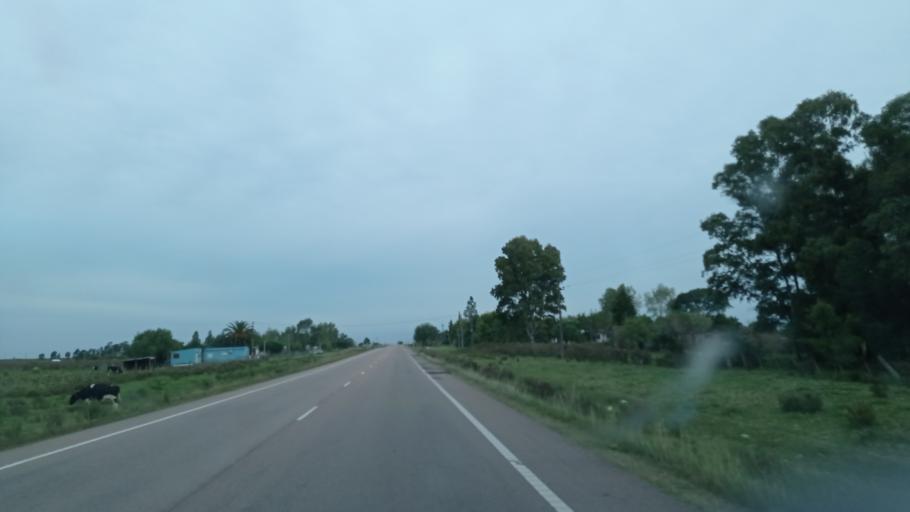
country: UY
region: Canelones
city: Tala
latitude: -34.4005
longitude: -55.8016
